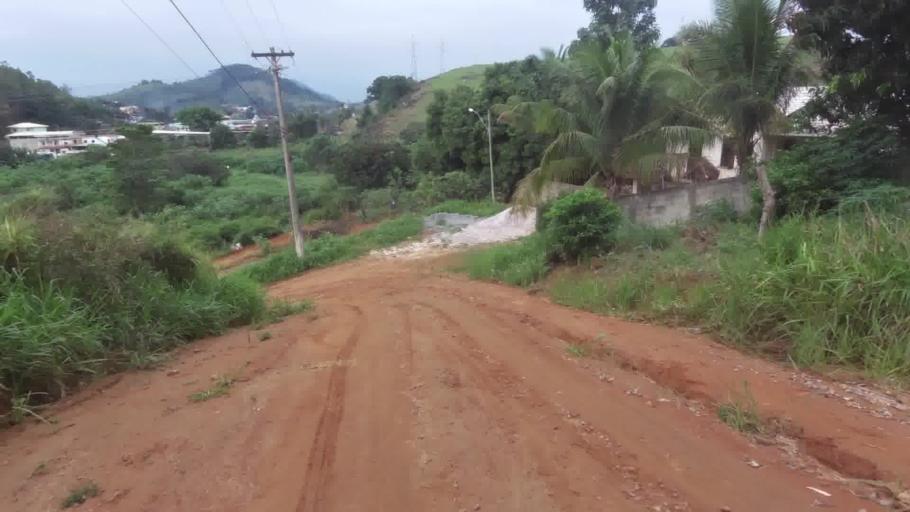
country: BR
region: Espirito Santo
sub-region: Iconha
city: Iconha
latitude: -20.7954
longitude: -40.8091
